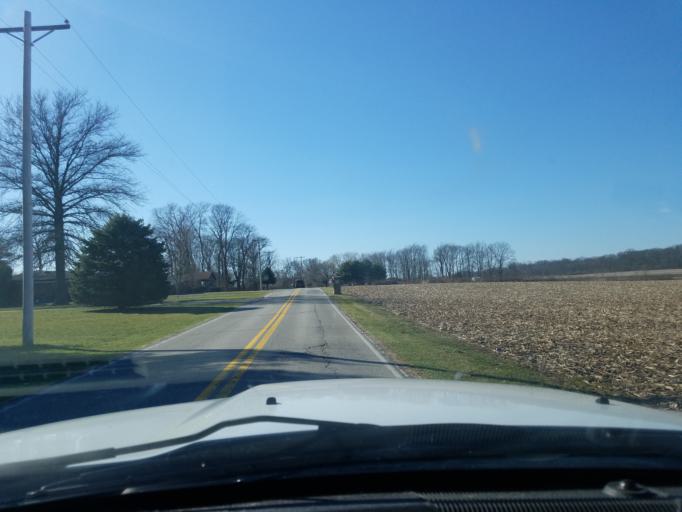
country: US
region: Indiana
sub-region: Johnson County
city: Franklin
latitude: 39.4967
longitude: -85.9920
